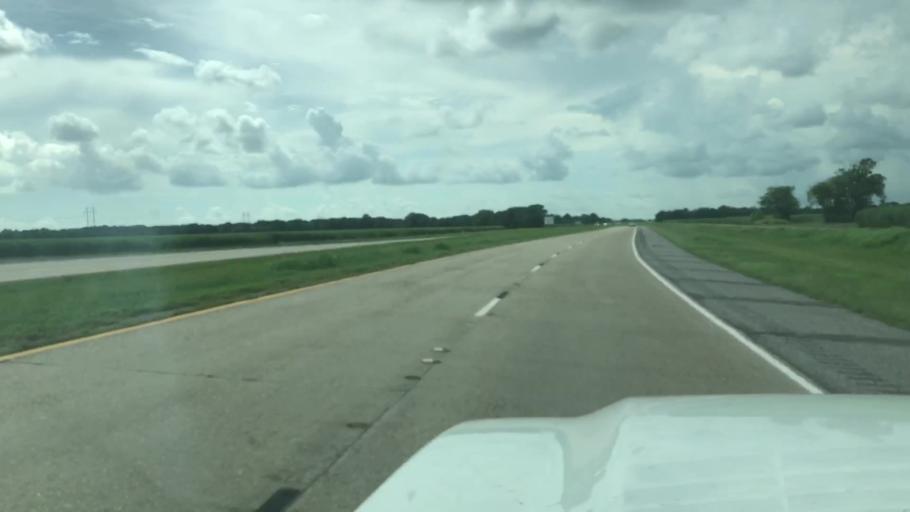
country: US
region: Louisiana
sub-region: Saint Mary Parish
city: Franklin
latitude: 29.7584
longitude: -91.4739
